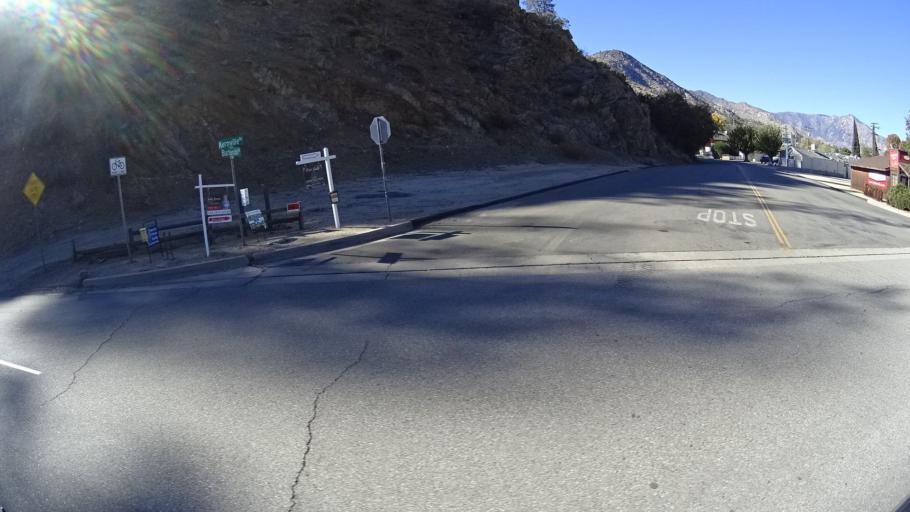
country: US
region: California
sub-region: Kern County
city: Kernville
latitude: 35.7539
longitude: -118.4255
